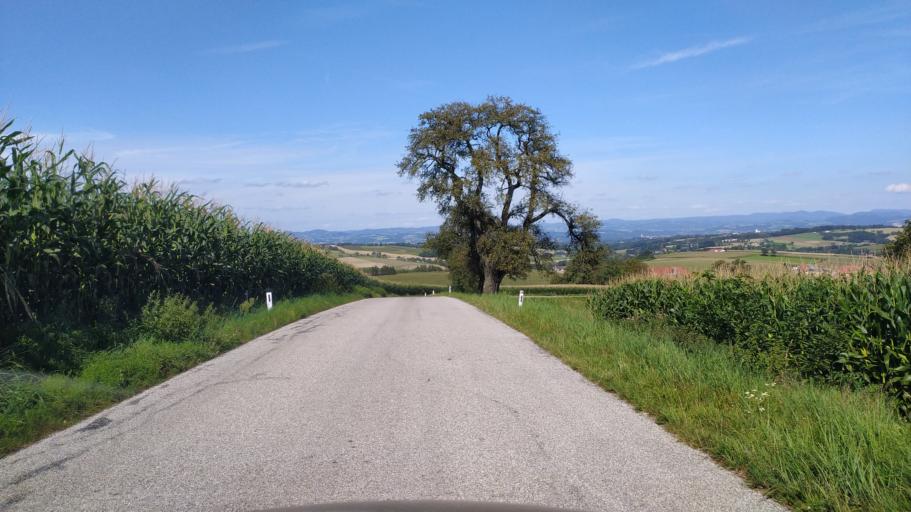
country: AT
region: Lower Austria
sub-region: Politischer Bezirk Amstetten
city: Strengberg
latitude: 48.1202
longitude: 14.6461
